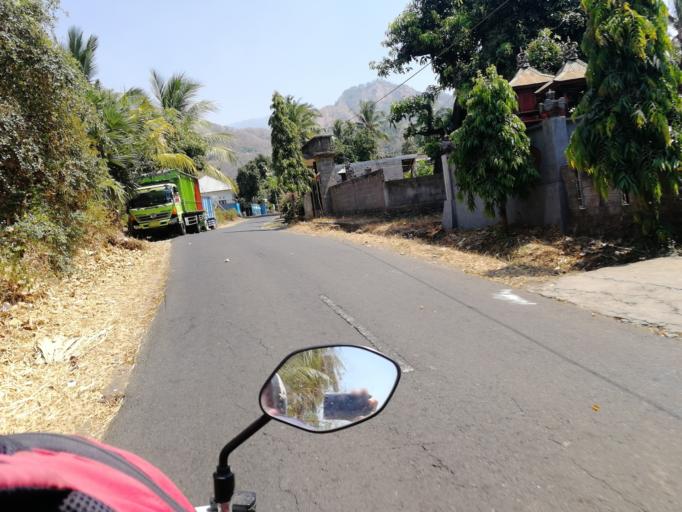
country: ID
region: Bali
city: Banjar Trunyan
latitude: -8.1236
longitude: 115.3286
